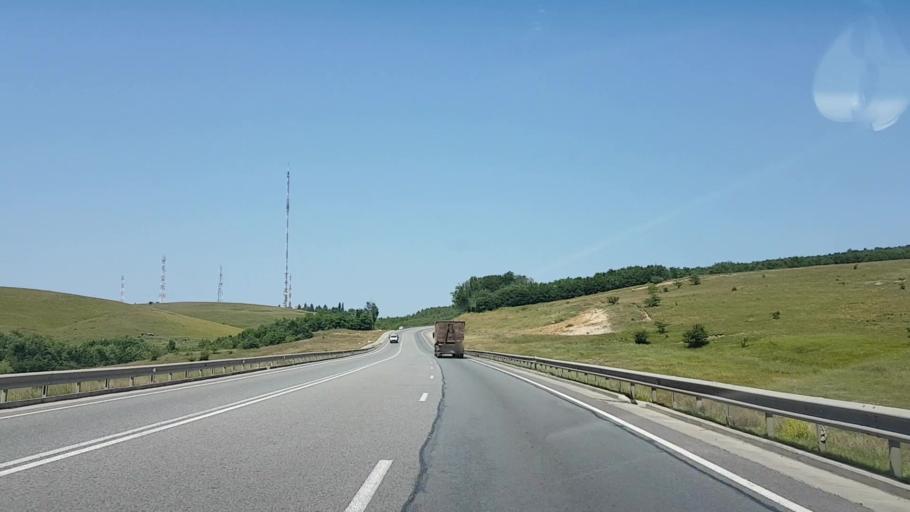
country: RO
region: Cluj
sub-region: Comuna Feleacu
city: Feleacu
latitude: 46.7028
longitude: 23.6414
